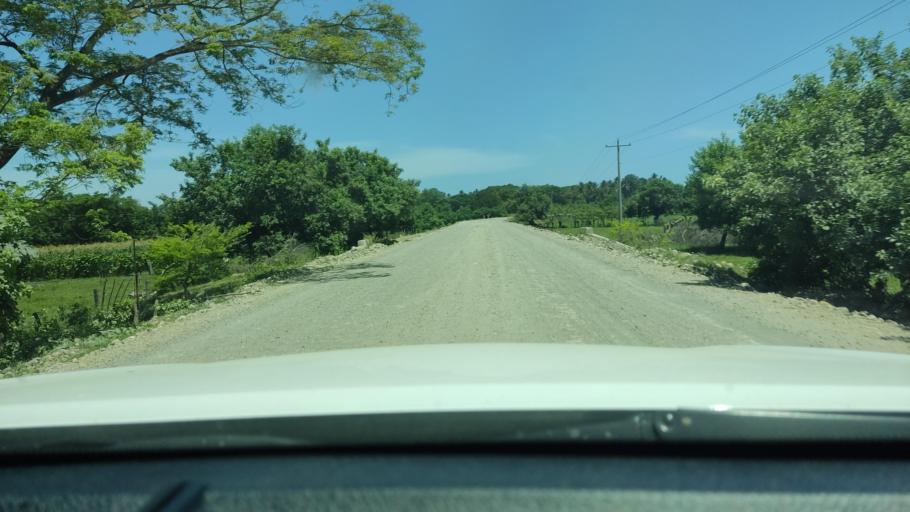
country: SV
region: Ahuachapan
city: San Francisco Menendez
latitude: 13.7950
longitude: -90.1174
